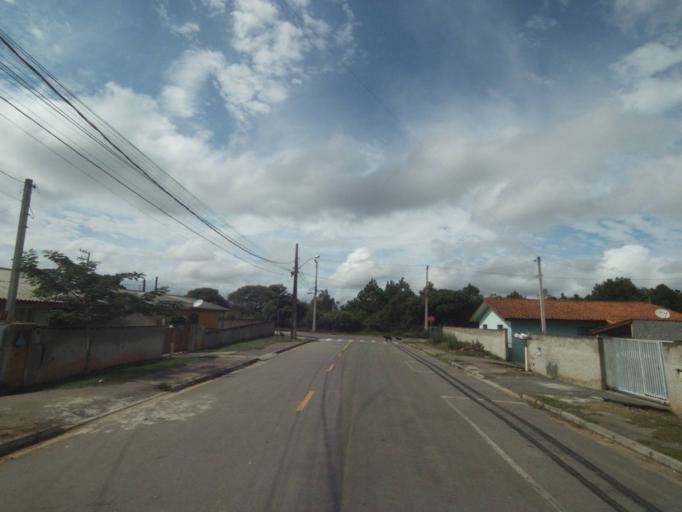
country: BR
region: Parana
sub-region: Quatro Barras
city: Quatro Barras
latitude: -25.3438
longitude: -49.0915
